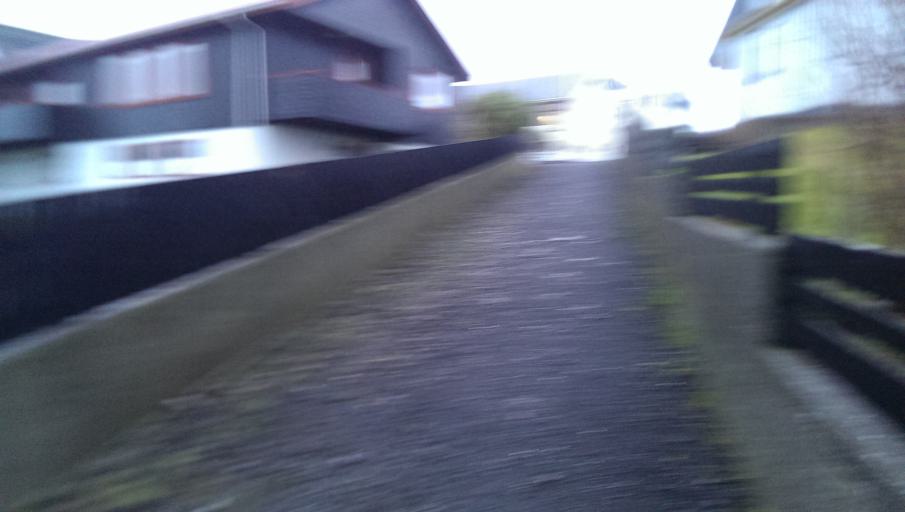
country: FO
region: Streymoy
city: Hoyvik
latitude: 62.0329
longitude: -6.7891
